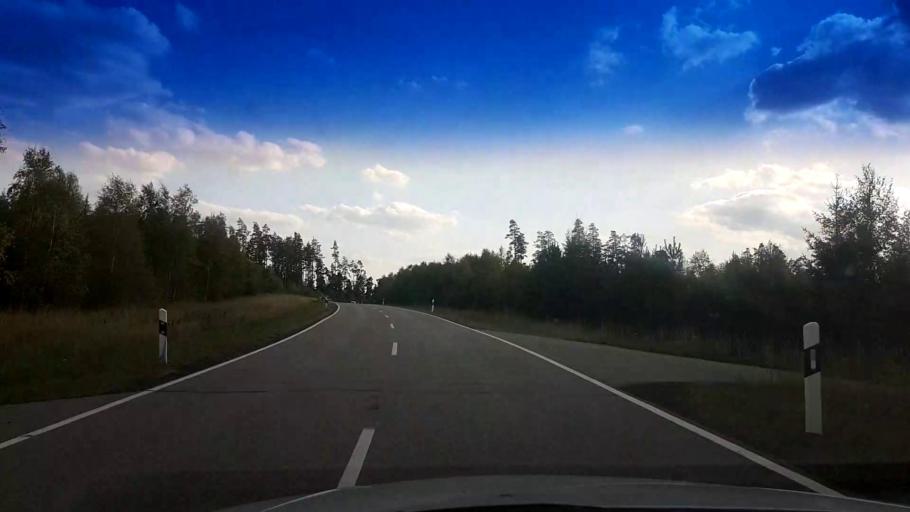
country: DE
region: Bavaria
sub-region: Upper Palatinate
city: Tirschenreuth
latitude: 49.8960
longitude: 12.3727
